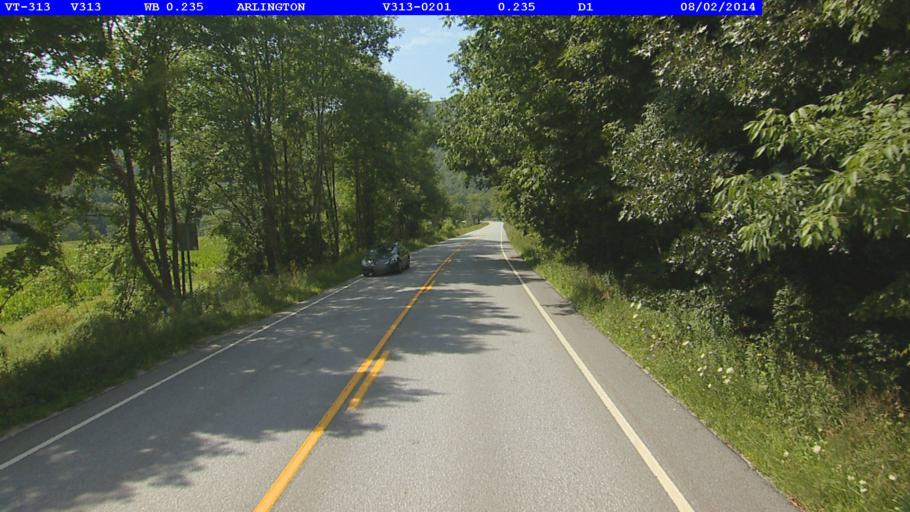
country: US
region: Vermont
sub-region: Bennington County
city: Arlington
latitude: 43.1069
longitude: -73.2607
